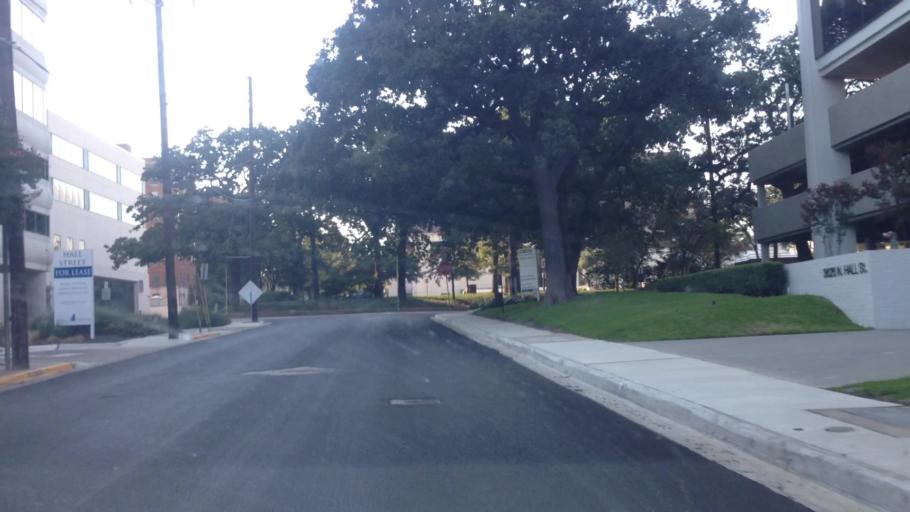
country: US
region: Texas
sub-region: Dallas County
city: Dallas
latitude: 32.8090
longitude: -96.8061
